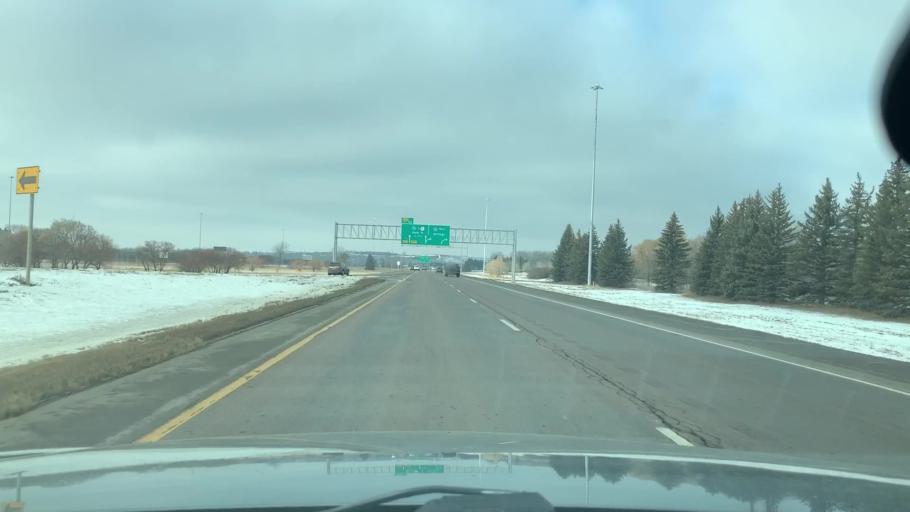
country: US
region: North Dakota
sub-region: Morton County
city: Mandan
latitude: 46.8226
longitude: -100.8425
